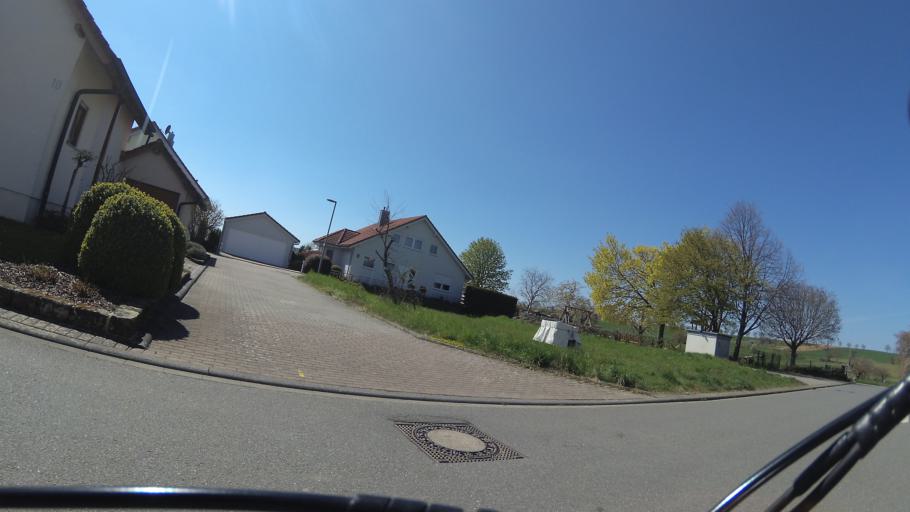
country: DE
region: Baden-Wuerttemberg
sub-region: Regierungsbezirk Stuttgart
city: Oedheim
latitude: 49.2387
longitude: 9.2239
